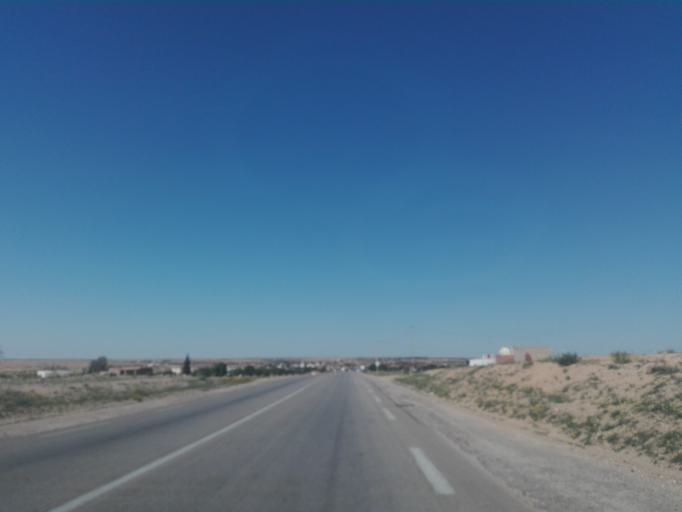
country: TN
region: Safaqis
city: Bi'r `Ali Bin Khalifah
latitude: 34.7404
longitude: 10.3916
